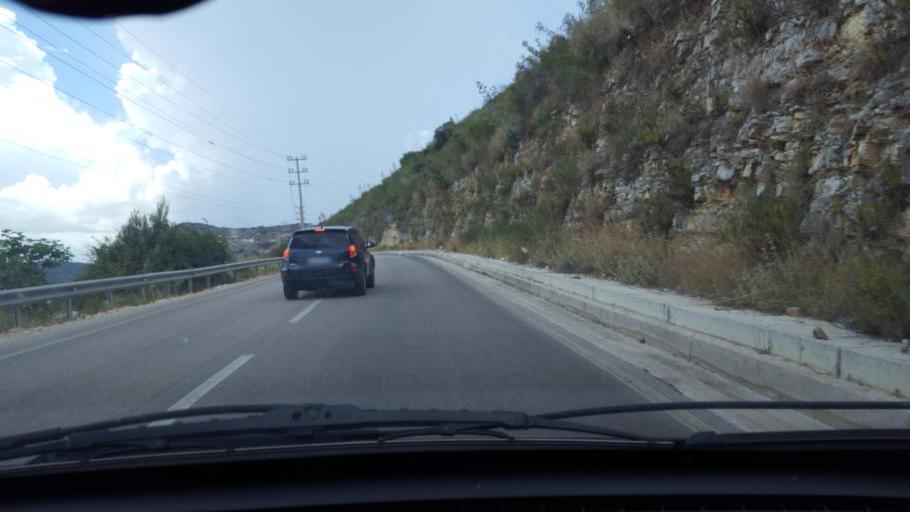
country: AL
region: Vlore
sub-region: Rrethi i Sarandes
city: Sarande
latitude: 39.8168
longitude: 20.0157
